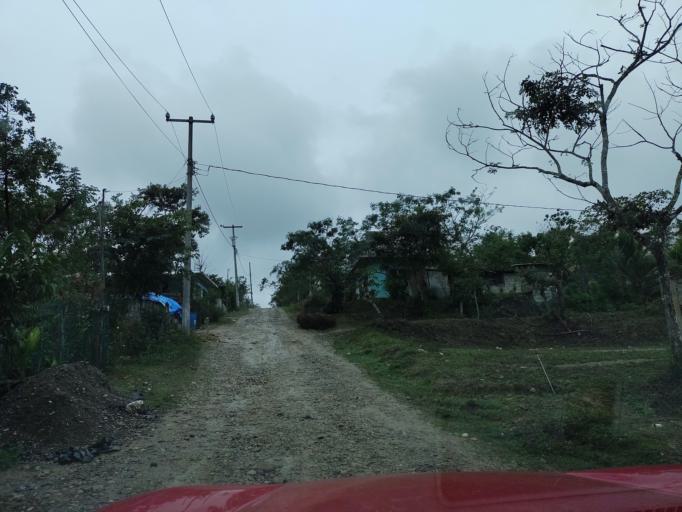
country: MX
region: Veracruz
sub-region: Papantla
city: El Chote
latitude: 20.3973
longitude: -97.3159
